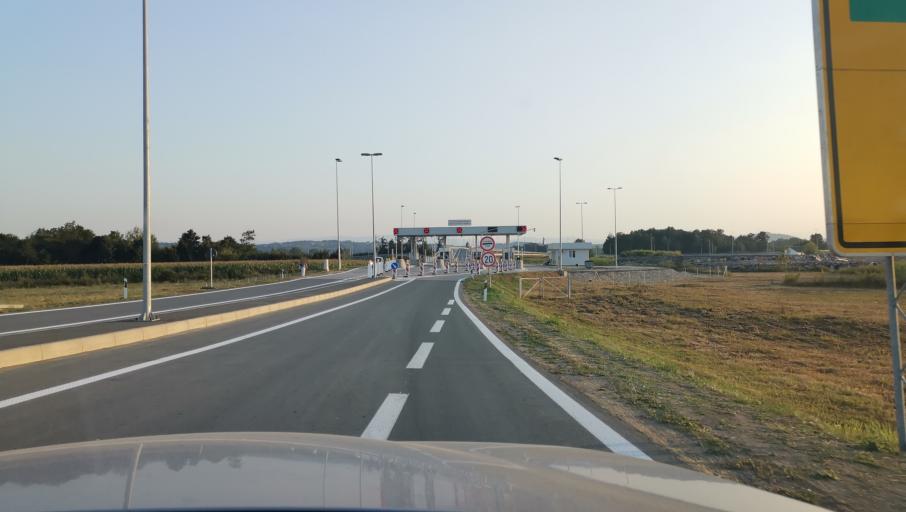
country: RS
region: Central Serbia
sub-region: Kolubarski Okrug
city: Lajkovac
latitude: 44.3609
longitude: 20.1316
